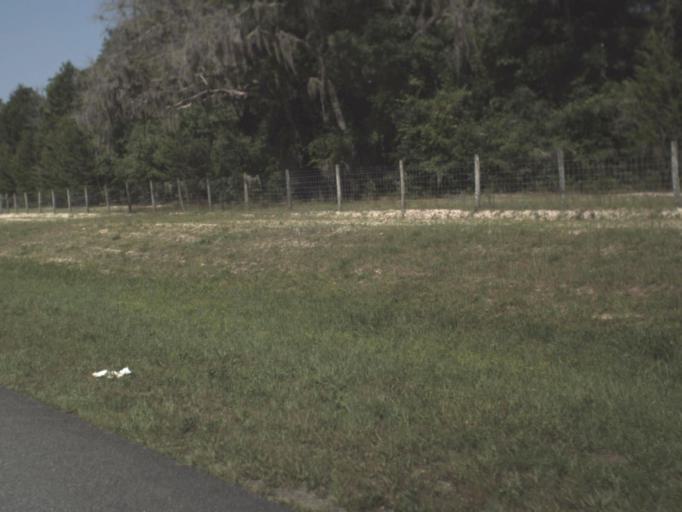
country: US
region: Florida
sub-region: Bradford County
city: Starke
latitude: 29.9609
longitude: -82.0183
